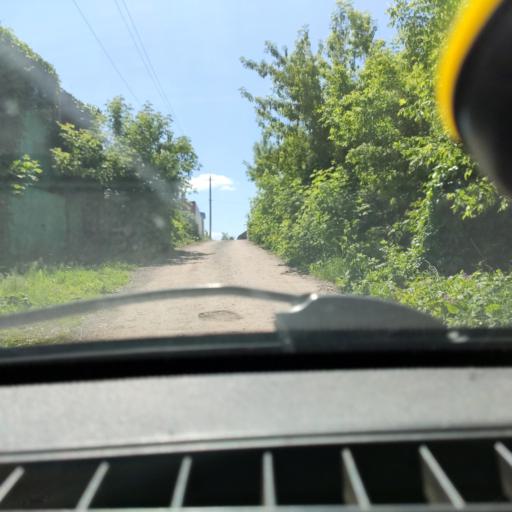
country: RU
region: Samara
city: Zhigulevsk
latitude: 53.3755
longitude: 49.5093
